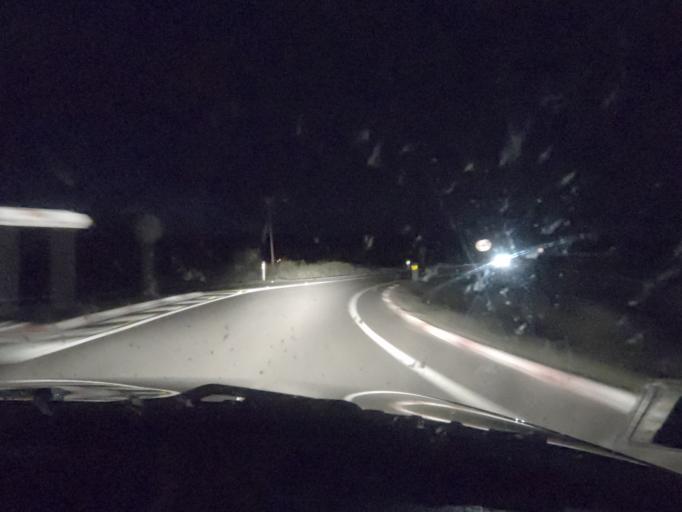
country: ES
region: Extremadura
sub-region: Provincia de Caceres
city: Moraleja
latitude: 40.0842
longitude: -6.6708
